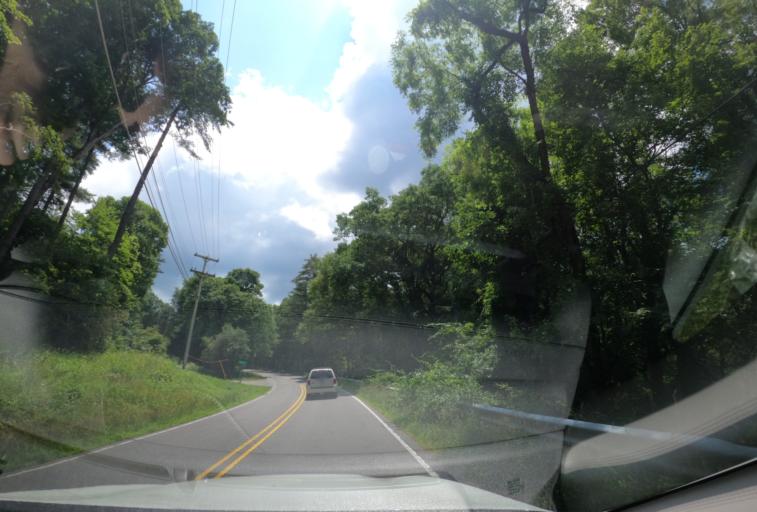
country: US
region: North Carolina
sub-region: Macon County
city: Franklin
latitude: 35.0623
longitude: -83.2193
